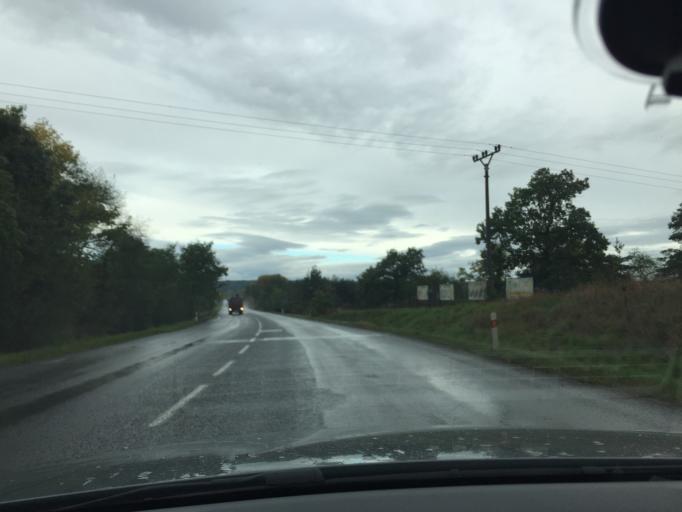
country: CZ
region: Central Bohemia
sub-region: Okres Melnik
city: Veltrusy
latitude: 50.2638
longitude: 14.3357
